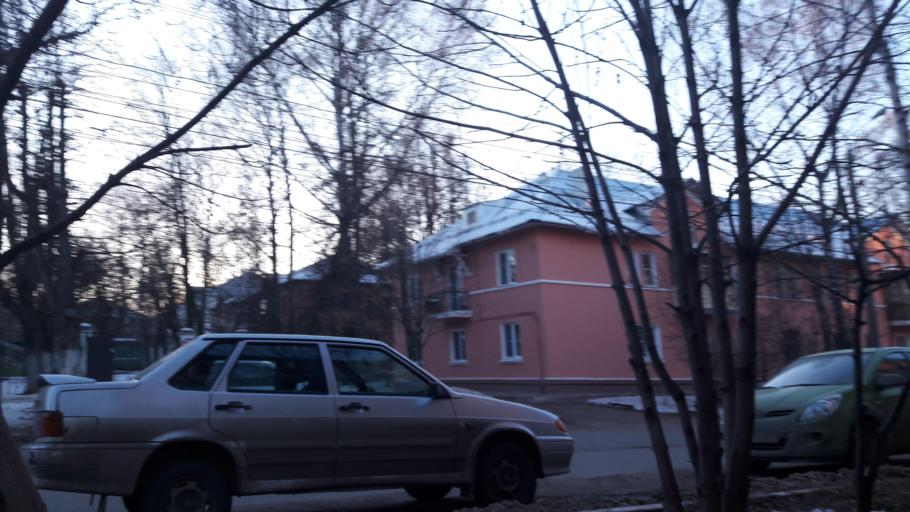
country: RU
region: Tula
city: Mendeleyevskiy
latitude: 54.1710
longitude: 37.5872
